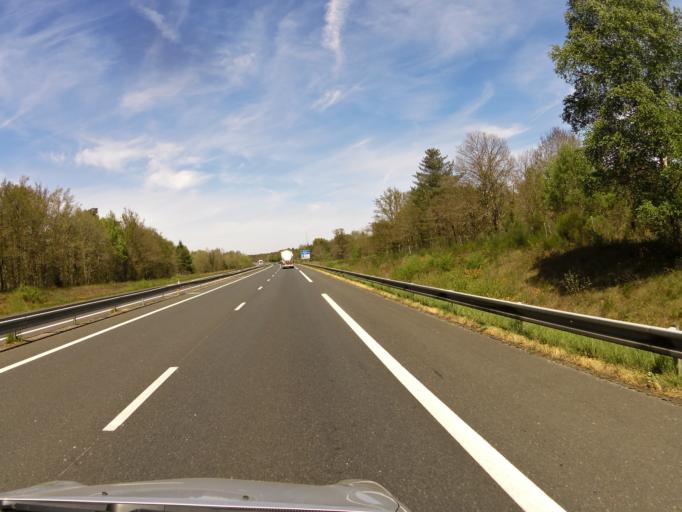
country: FR
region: Centre
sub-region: Departement du Loir-et-Cher
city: Nouan-le-Fuzelier
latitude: 47.5397
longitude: 2.0067
